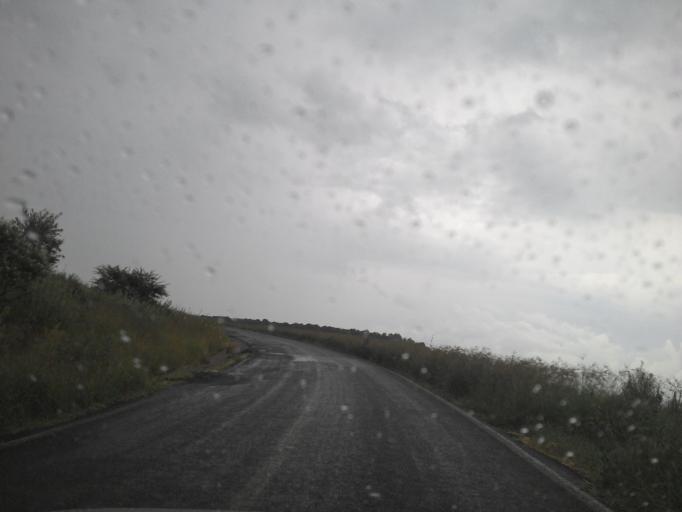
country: MX
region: Jalisco
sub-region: Arandas
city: Santiaguito (Santiaguito de Velazquez)
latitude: 20.7861
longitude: -102.2794
